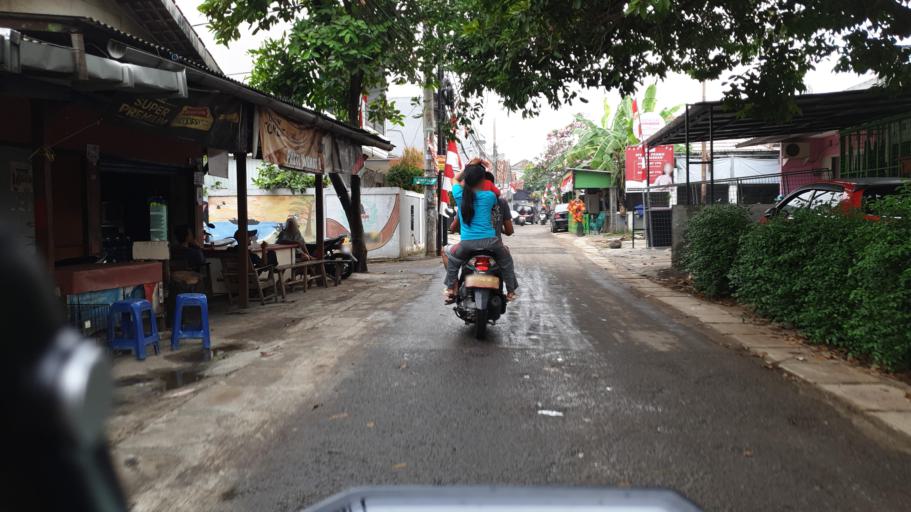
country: ID
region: West Java
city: Pamulang
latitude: -6.3342
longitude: 106.7698
